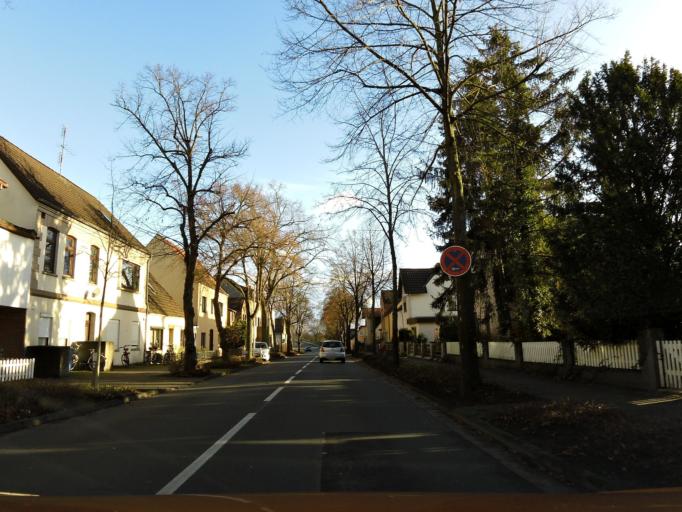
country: DE
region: Lower Saxony
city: Verden
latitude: 52.9129
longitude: 9.2381
